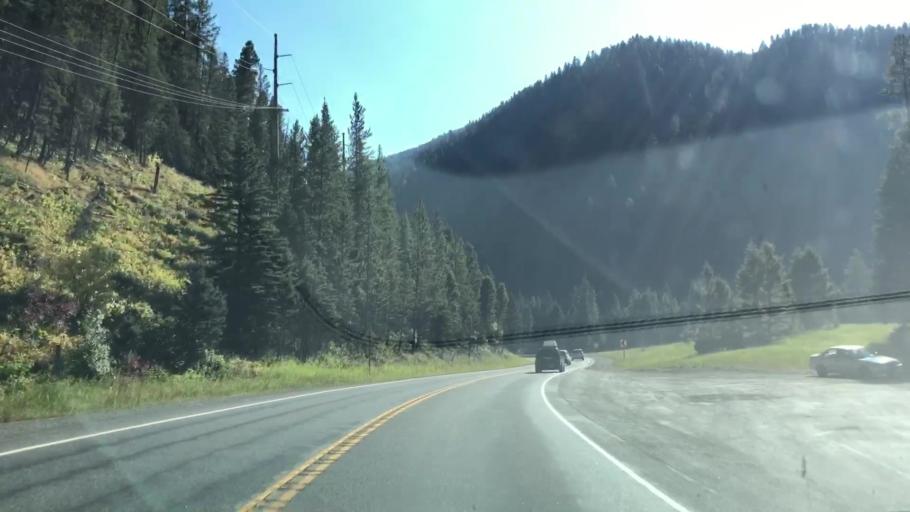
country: US
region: Montana
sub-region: Gallatin County
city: Big Sky
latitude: 45.3767
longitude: -111.1741
